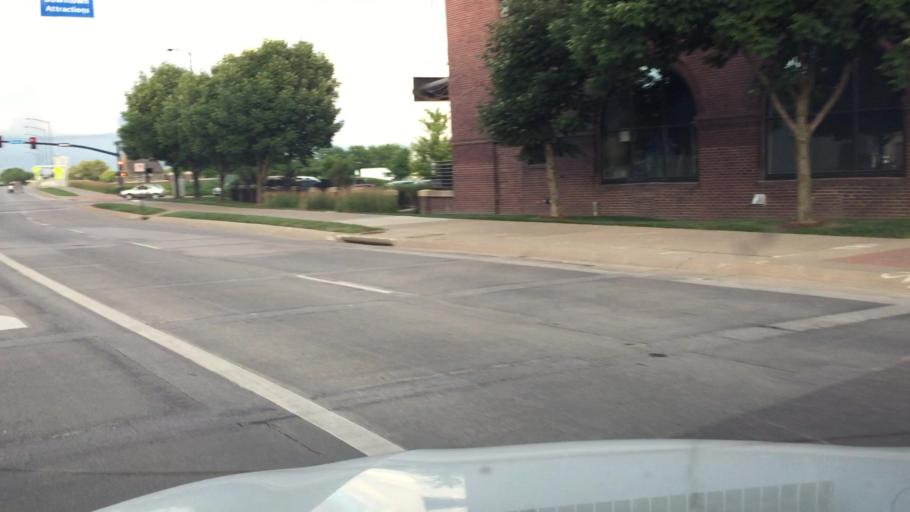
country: US
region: Iowa
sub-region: Polk County
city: Des Moines
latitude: 41.5822
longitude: -93.6192
